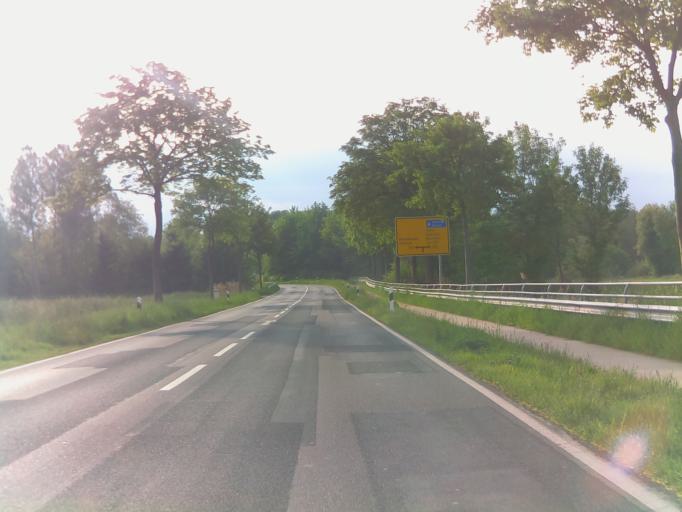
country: DE
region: Lower Saxony
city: Kalefeld
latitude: 51.7933
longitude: 10.0409
